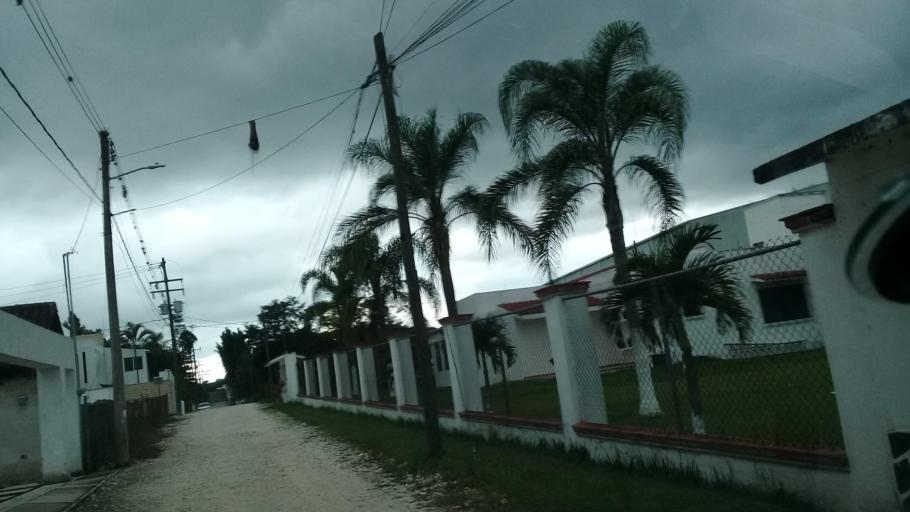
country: MX
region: Veracruz
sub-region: Emiliano Zapata
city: Dos Rios
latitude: 19.4889
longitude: -96.8063
